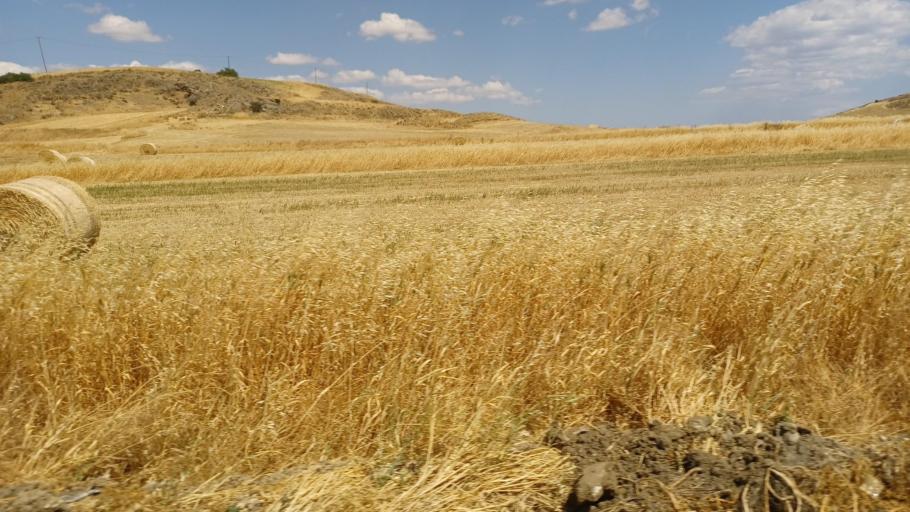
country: CY
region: Larnaka
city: Troulloi
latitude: 35.0199
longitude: 33.6116
